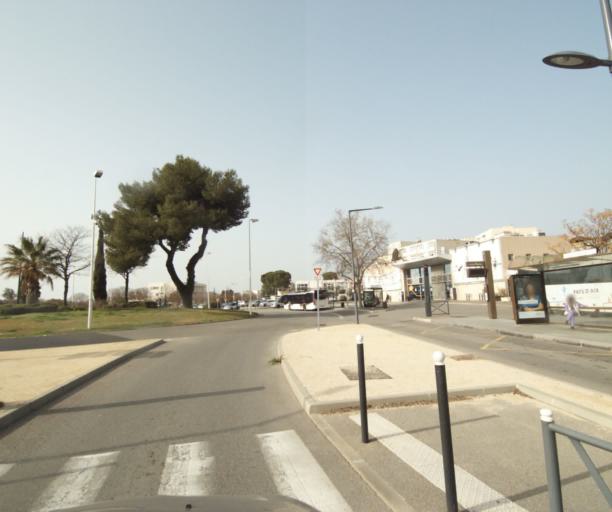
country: FR
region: Provence-Alpes-Cote d'Azur
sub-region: Departement des Bouches-du-Rhone
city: Vitrolles
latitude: 43.4462
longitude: 5.2490
